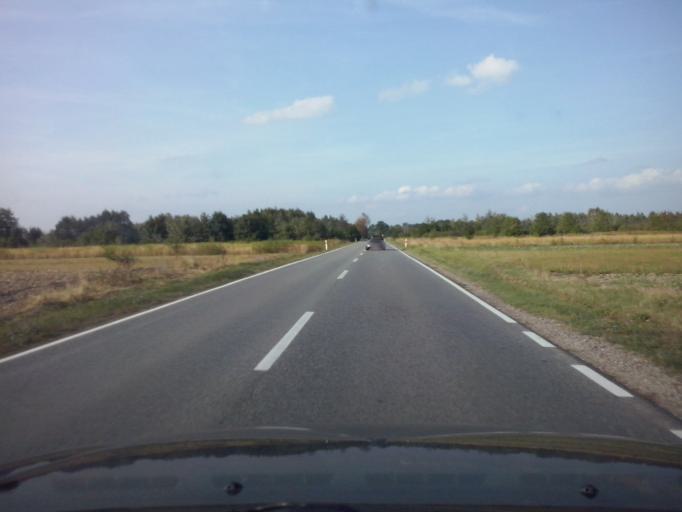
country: PL
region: Subcarpathian Voivodeship
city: Nowa Sarzyna
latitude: 50.3599
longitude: 22.3207
